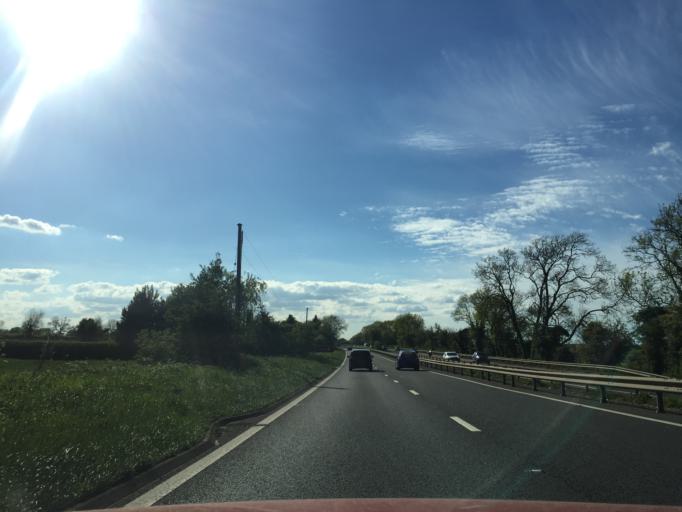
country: GB
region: England
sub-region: Warwickshire
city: Ryton on Dunsmore
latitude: 52.3623
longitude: -1.4144
